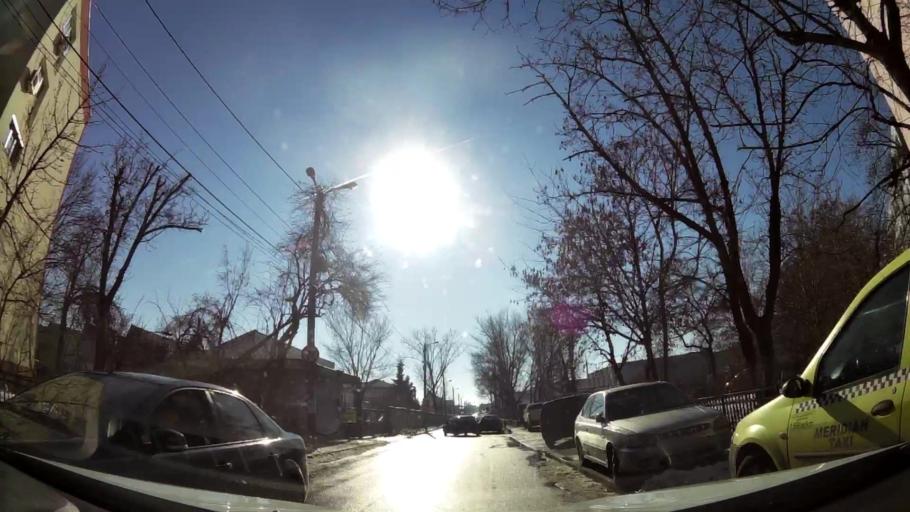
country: RO
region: Bucuresti
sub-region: Municipiul Bucuresti
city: Bucuresti
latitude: 44.4030
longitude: 26.0600
